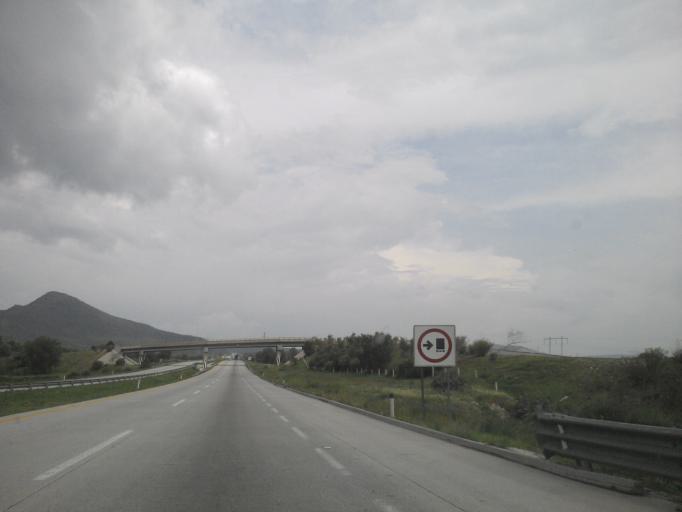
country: MX
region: Hidalgo
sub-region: Atitalaquia
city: Tezoquipa
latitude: 20.0499
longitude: -99.1883
